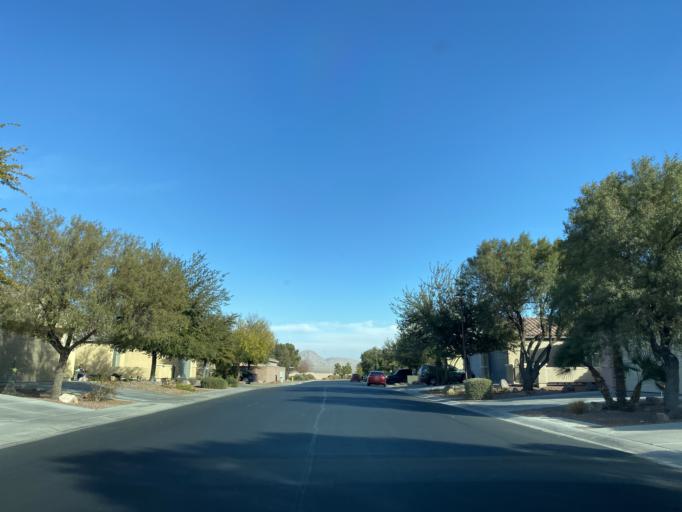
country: US
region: Nevada
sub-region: Clark County
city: North Las Vegas
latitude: 36.3206
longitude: -115.2482
